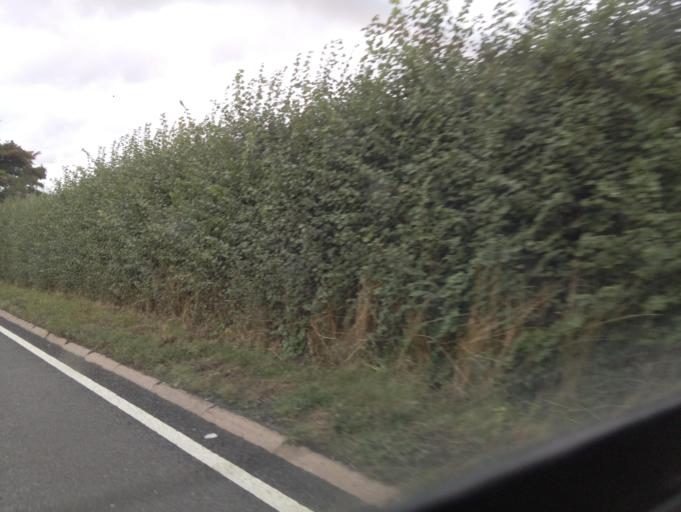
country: GB
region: England
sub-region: Worcestershire
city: Droitwich
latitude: 52.2954
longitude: -2.1730
